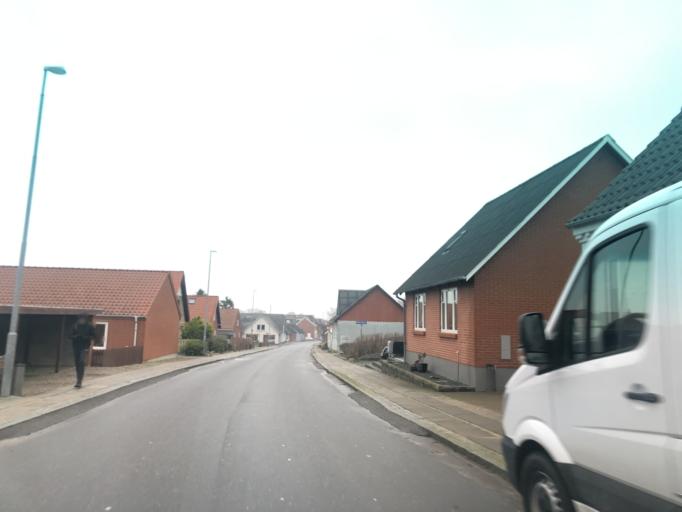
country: DK
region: North Denmark
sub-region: Thisted Kommune
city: Hurup
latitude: 56.7468
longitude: 8.4196
